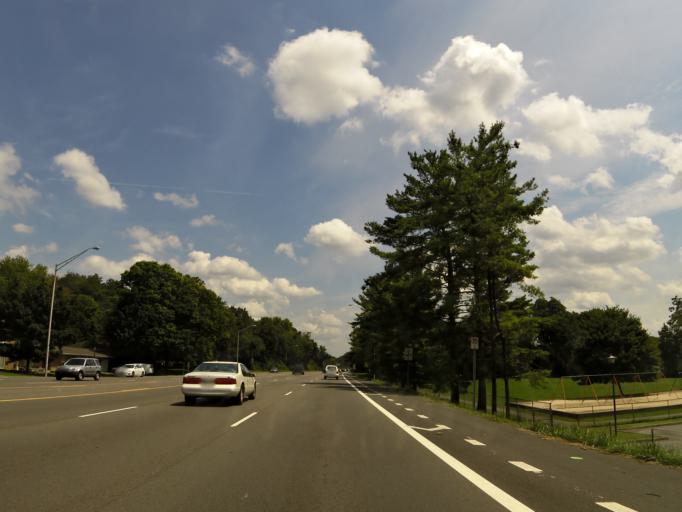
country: US
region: Tennessee
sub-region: Sullivan County
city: Kingsport
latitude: 36.5596
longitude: -82.5648
